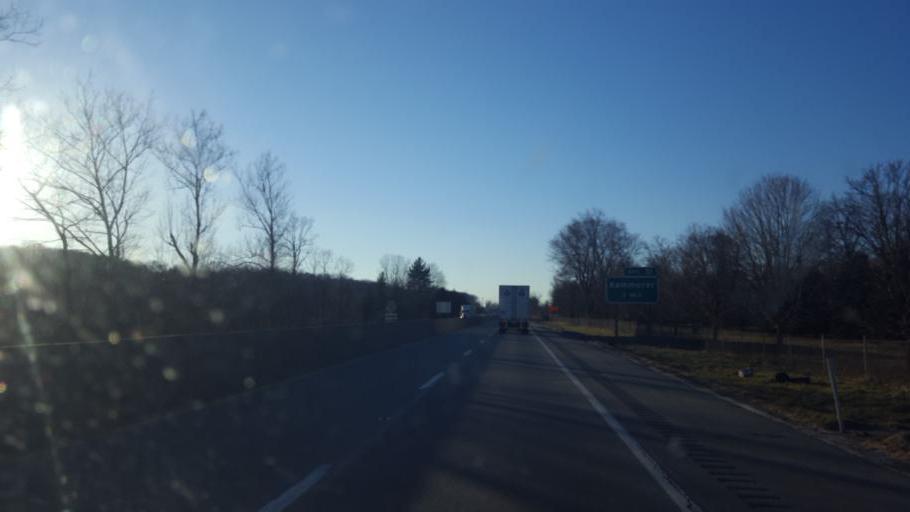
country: US
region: Pennsylvania
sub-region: Washington County
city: Bentleyville
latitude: 40.1391
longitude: -80.0167
